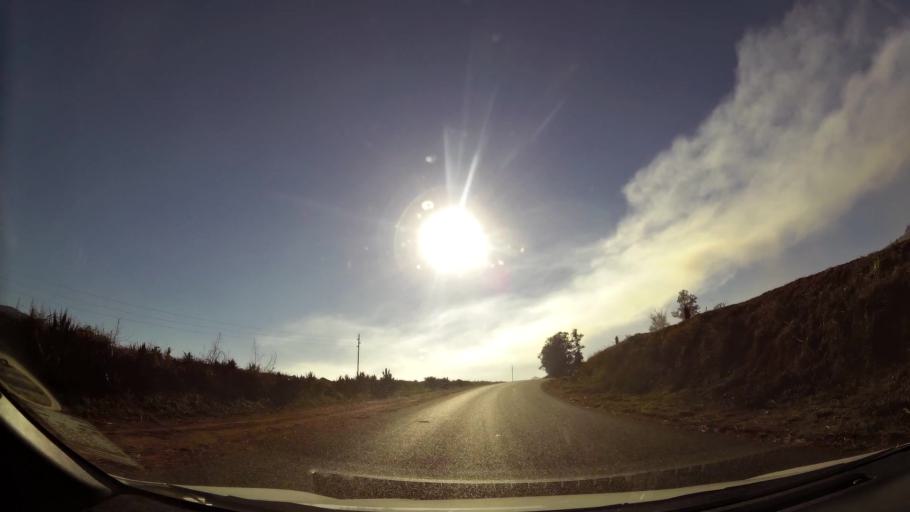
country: ZA
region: Limpopo
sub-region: Mopani District Municipality
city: Tzaneen
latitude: -23.9047
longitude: 30.0636
